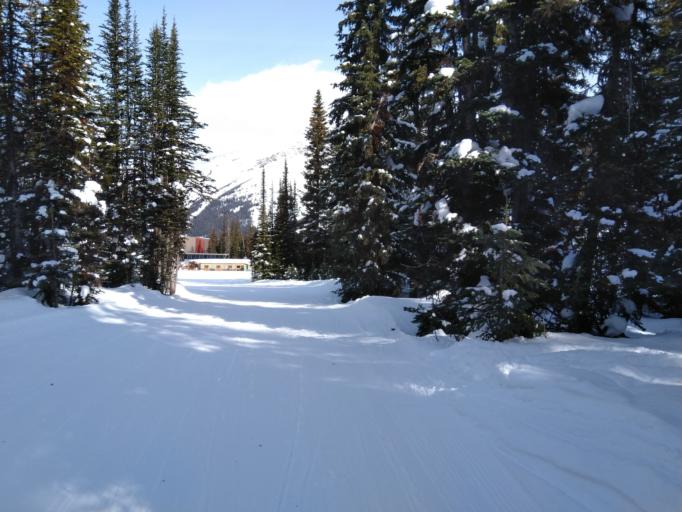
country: CA
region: Alberta
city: Banff
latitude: 51.0935
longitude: -115.7709
